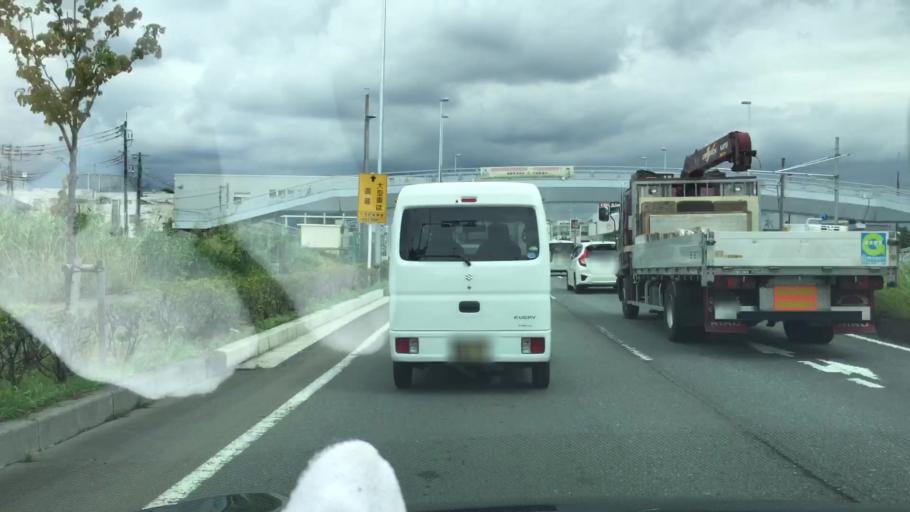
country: JP
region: Saitama
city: Ageoshimo
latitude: 35.9244
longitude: 139.5777
